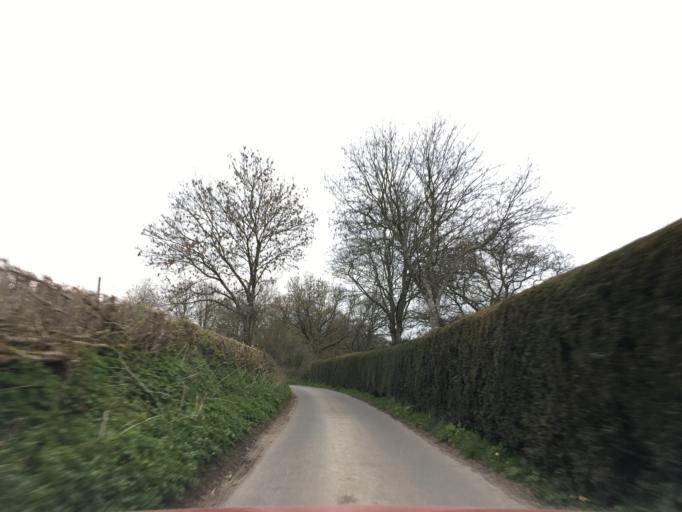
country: GB
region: England
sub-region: Gloucestershire
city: Wotton-under-Edge
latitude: 51.6059
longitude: -2.3188
